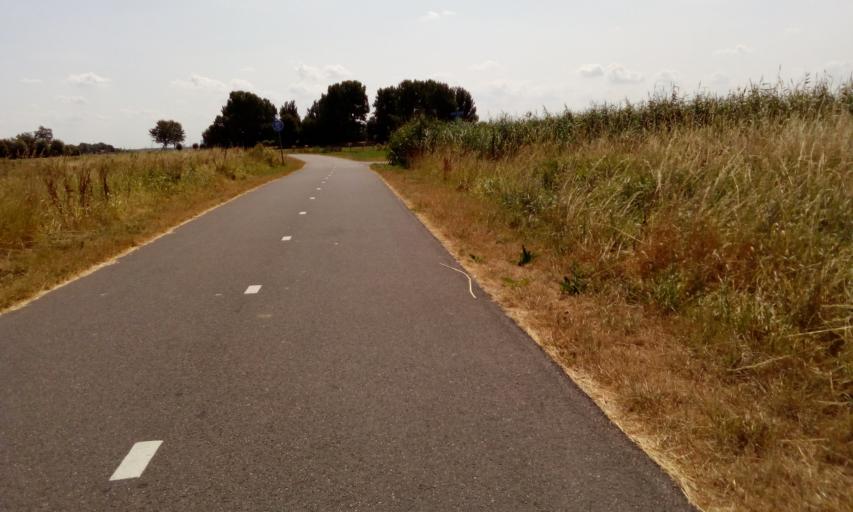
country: NL
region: South Holland
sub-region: Gemeente Delft
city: Delft
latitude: 51.9714
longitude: 4.3179
